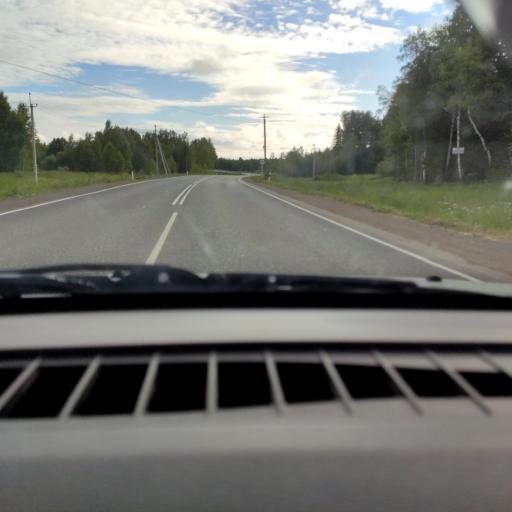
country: RU
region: Perm
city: Kungur
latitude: 57.3303
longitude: 56.9613
